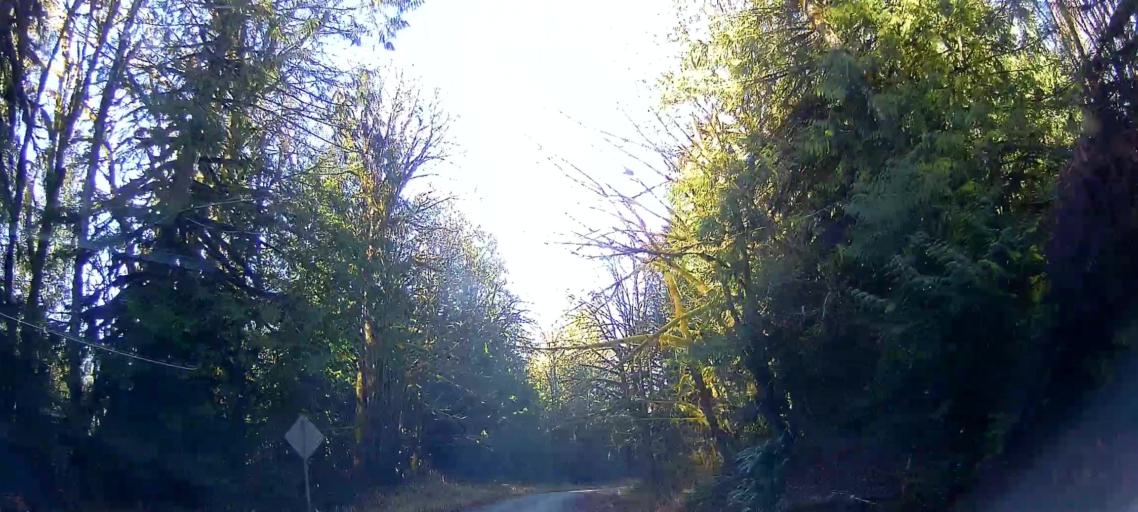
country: US
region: Washington
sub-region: Snohomish County
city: Darrington
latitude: 48.5464
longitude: -121.7291
